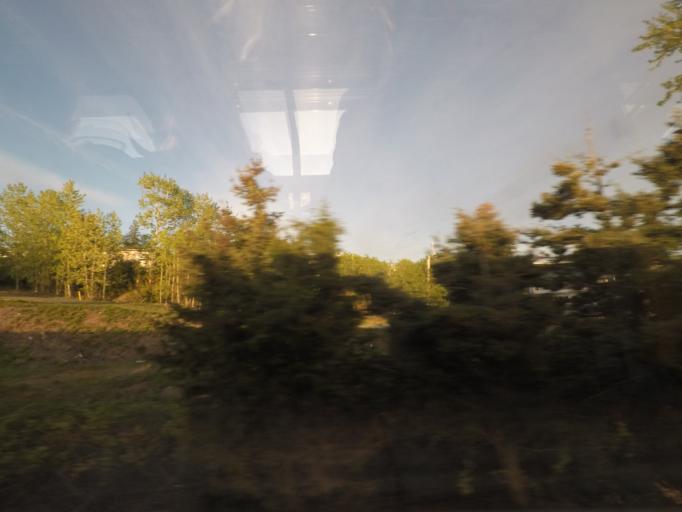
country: US
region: Washington
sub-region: Whatcom County
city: Bellingham
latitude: 48.7234
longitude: -122.5059
